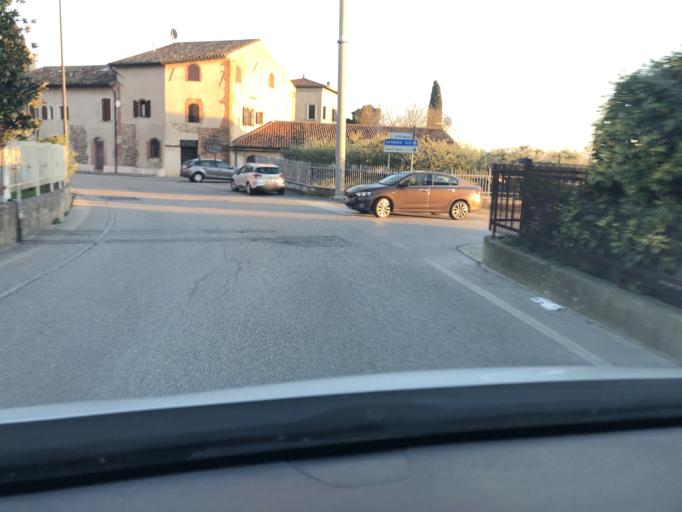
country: IT
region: Veneto
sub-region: Provincia di Verona
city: Sona
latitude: 45.4505
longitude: 10.8186
